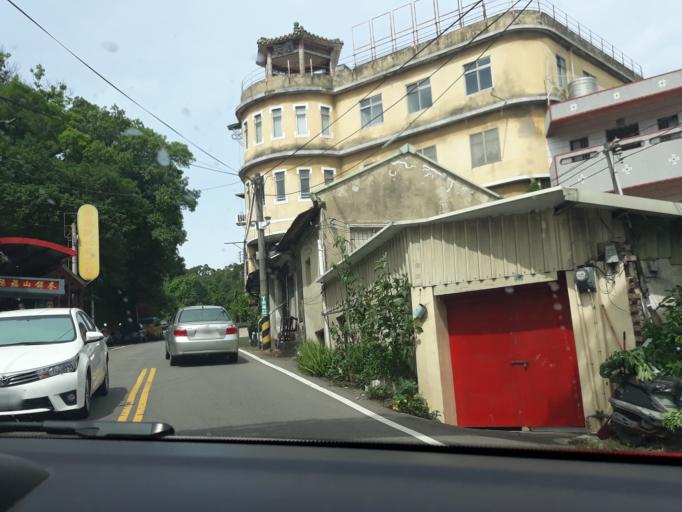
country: TW
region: Taiwan
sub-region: Miaoli
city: Miaoli
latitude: 24.5551
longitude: 120.8140
